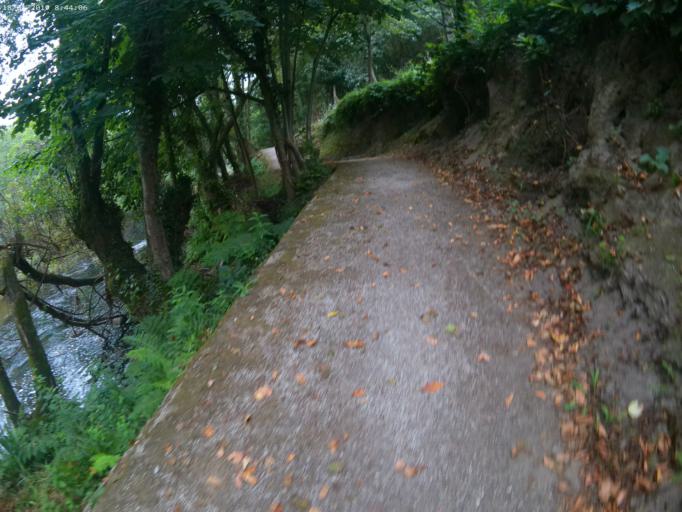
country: PT
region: Viana do Castelo
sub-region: Ponte da Barca
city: Ponte da Barca
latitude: 41.8112
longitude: -8.4301
